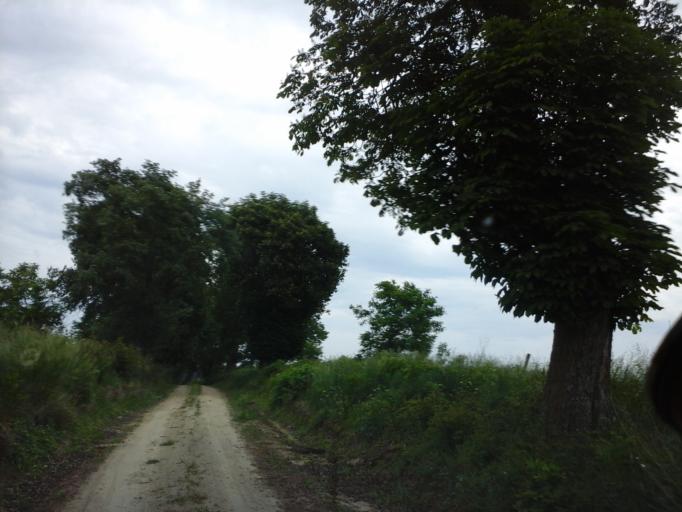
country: PL
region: West Pomeranian Voivodeship
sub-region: Powiat choszczenski
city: Krzecin
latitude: 53.1424
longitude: 15.5754
